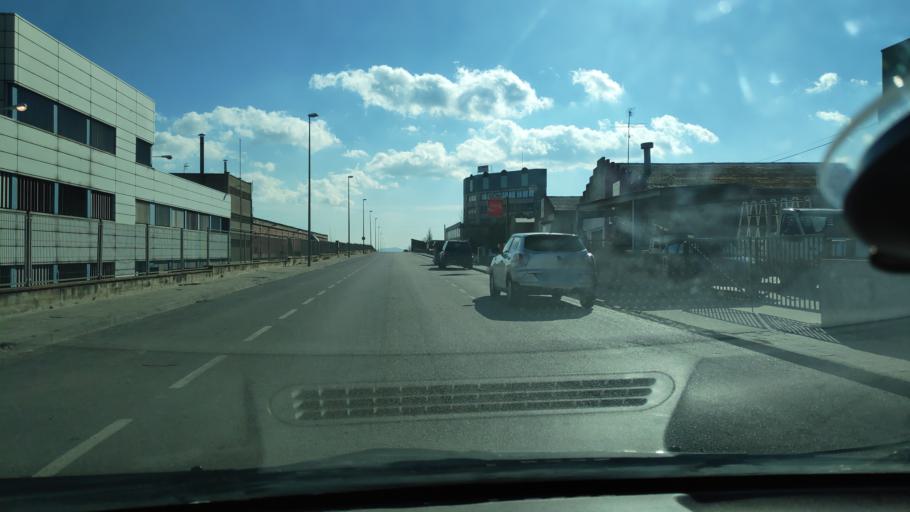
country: ES
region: Catalonia
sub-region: Provincia de Barcelona
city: Sant Quirze del Valles
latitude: 41.5421
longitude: 2.0755
